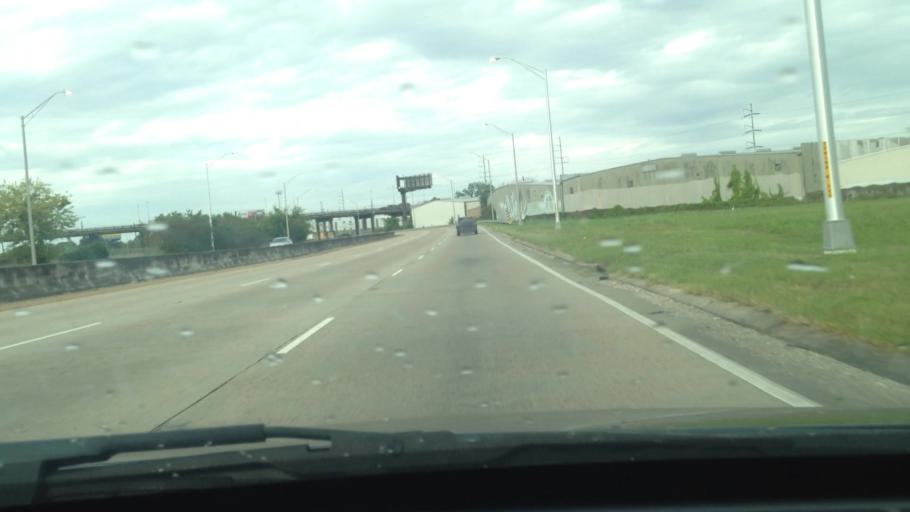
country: US
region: Louisiana
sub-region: Jefferson Parish
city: Jefferson
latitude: 29.9708
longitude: -90.1531
